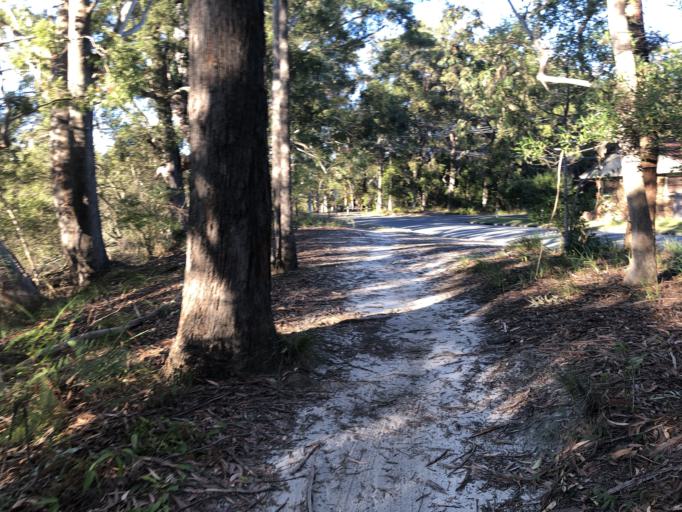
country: AU
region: New South Wales
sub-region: Coffs Harbour
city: Coffs Harbour
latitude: -30.2899
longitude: 153.1243
